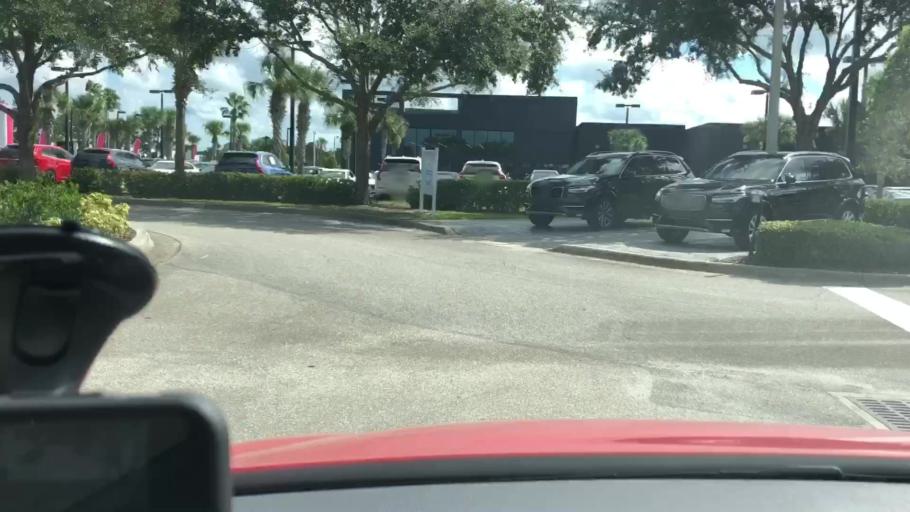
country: US
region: Florida
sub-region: Volusia County
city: Holly Hill
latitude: 29.2077
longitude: -81.1005
